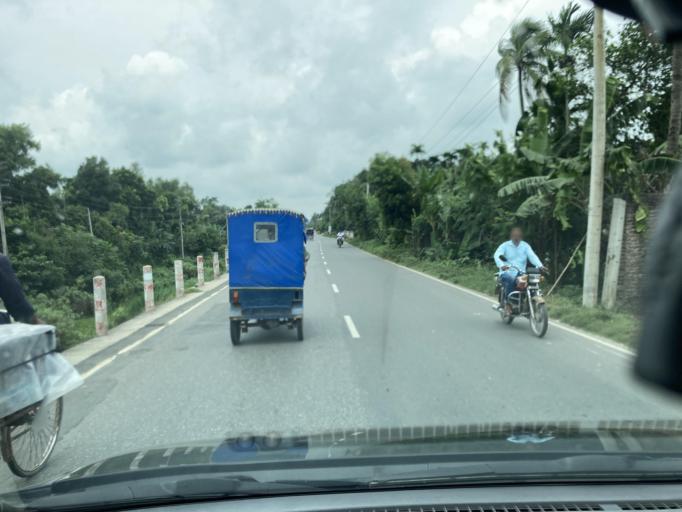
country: BD
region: Dhaka
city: Azimpur
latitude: 23.8057
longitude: 90.2143
